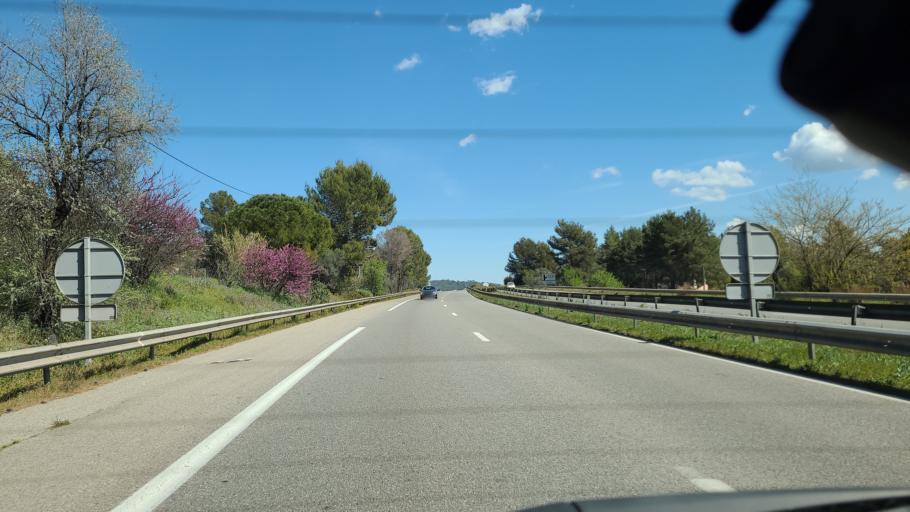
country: FR
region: Provence-Alpes-Cote d'Azur
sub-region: Departement du Var
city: Sollies-Pont
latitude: 43.2089
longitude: 6.0531
